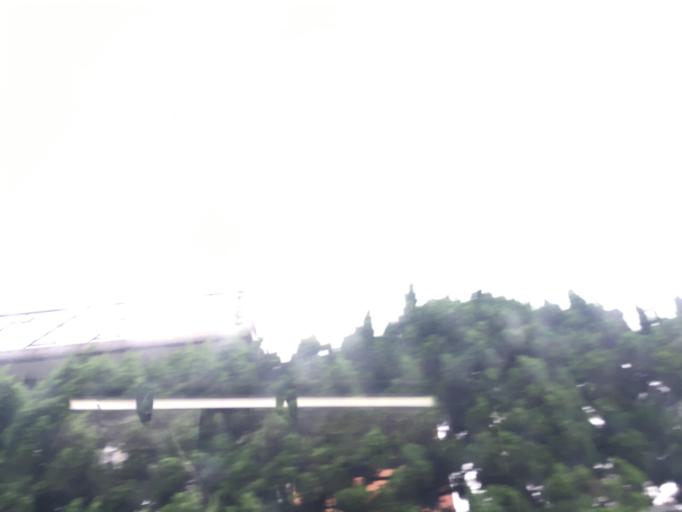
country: TW
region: Taipei
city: Taipei
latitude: 25.1326
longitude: 121.5285
